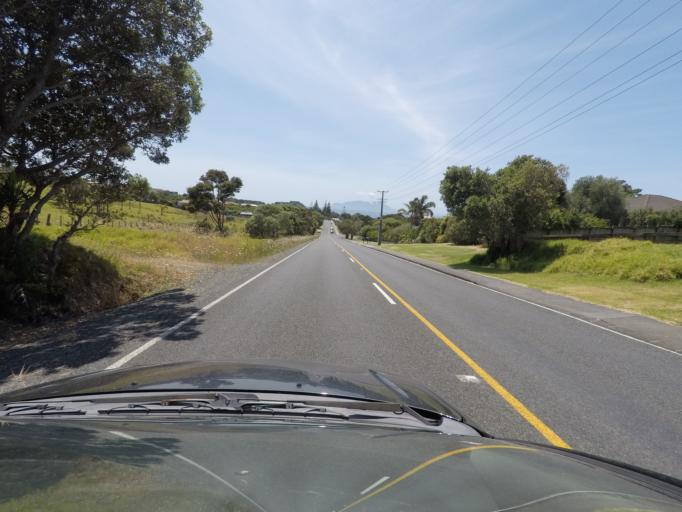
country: NZ
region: Auckland
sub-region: Auckland
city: Warkworth
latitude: -36.2947
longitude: 174.7994
